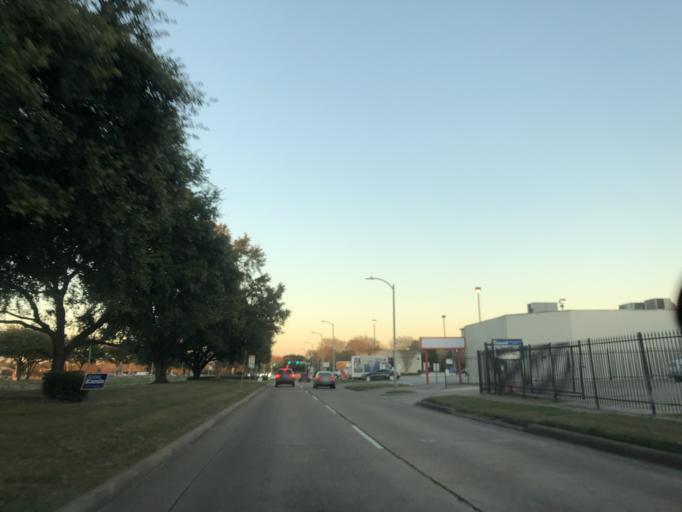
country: US
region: Texas
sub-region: Harris County
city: Bellaire
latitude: 29.6762
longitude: -95.4790
